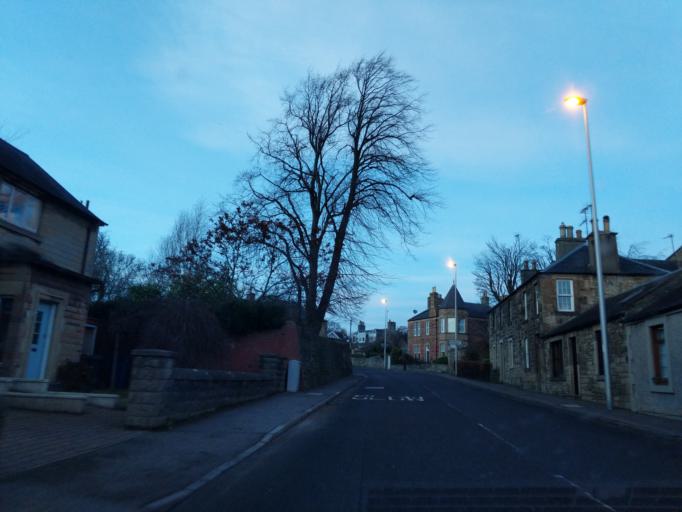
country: GB
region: Scotland
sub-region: Midlothian
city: Bonnyrigg
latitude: 55.8788
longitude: -3.1081
